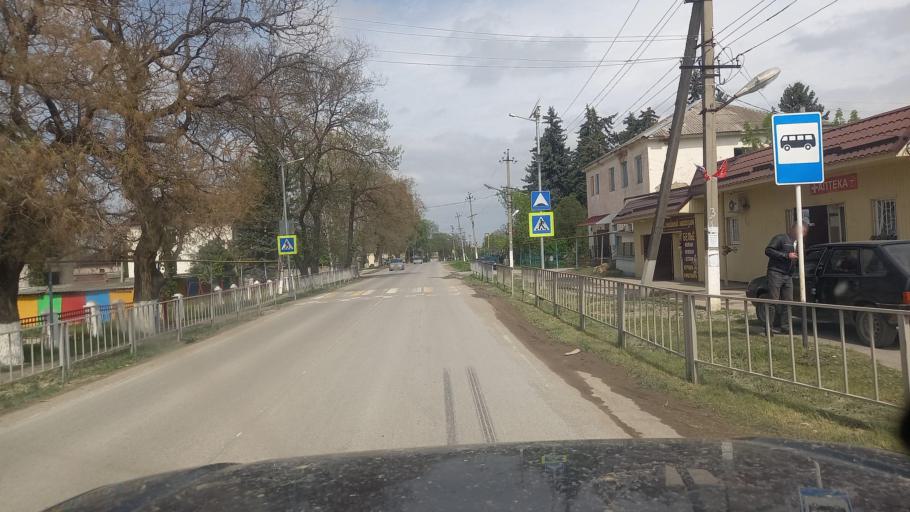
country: RU
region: Kabardino-Balkariya
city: Sarmakovo
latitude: 43.7417
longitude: 43.1921
